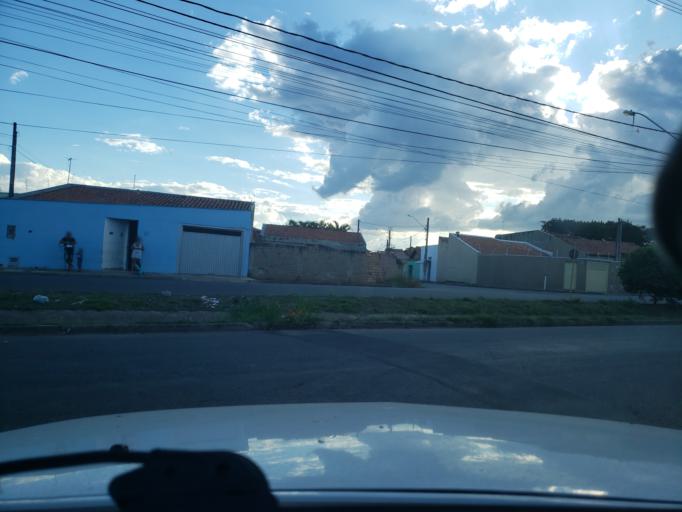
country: BR
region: Sao Paulo
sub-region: Moji-Guacu
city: Mogi-Gaucu
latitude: -22.3299
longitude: -46.9256
